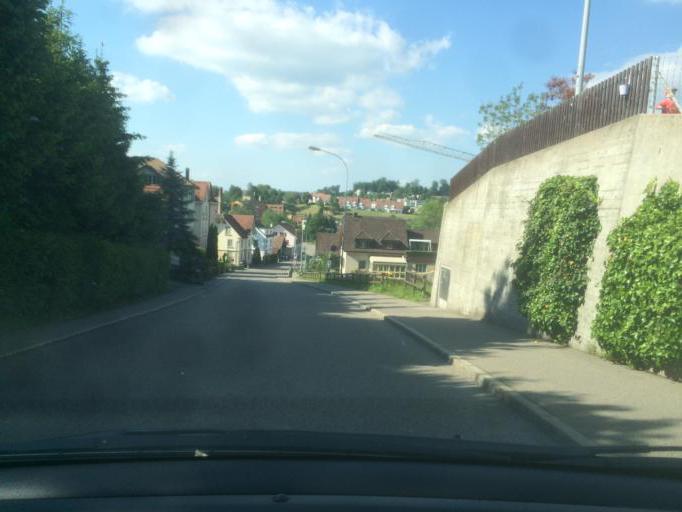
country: CH
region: Zurich
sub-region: Bezirk Uster
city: Uster / Nossikon
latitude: 47.3423
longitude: 8.7296
